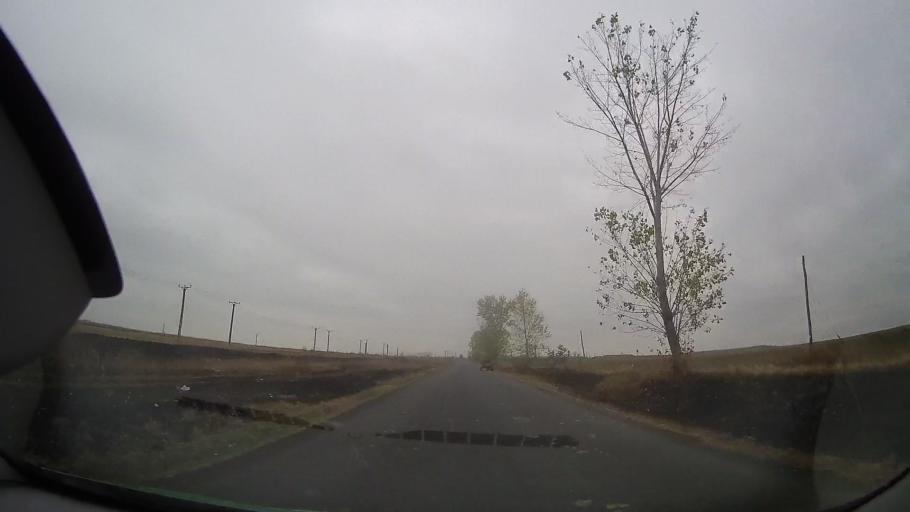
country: RO
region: Braila
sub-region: Comuna Ciocile
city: Ciocile
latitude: 44.8124
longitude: 27.2658
